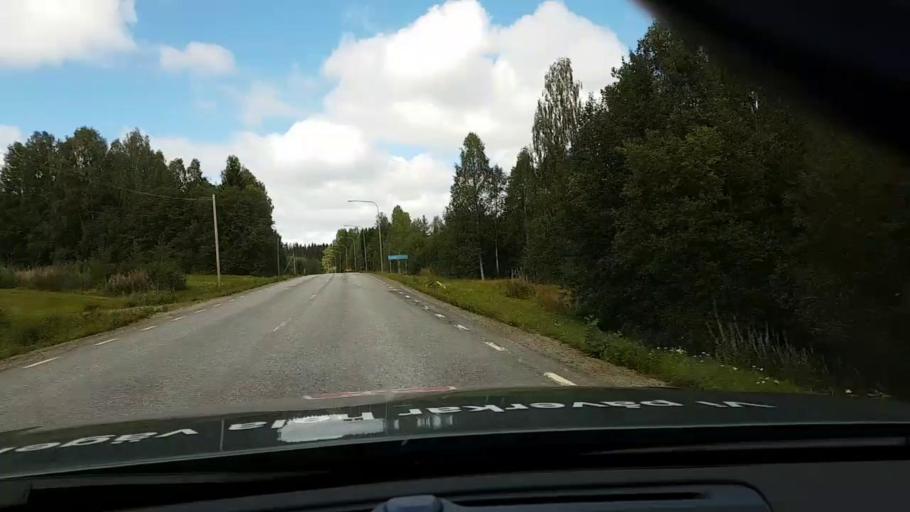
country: SE
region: Vaesternorrland
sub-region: OErnskoeldsviks Kommun
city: Bredbyn
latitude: 63.4877
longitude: 18.0847
